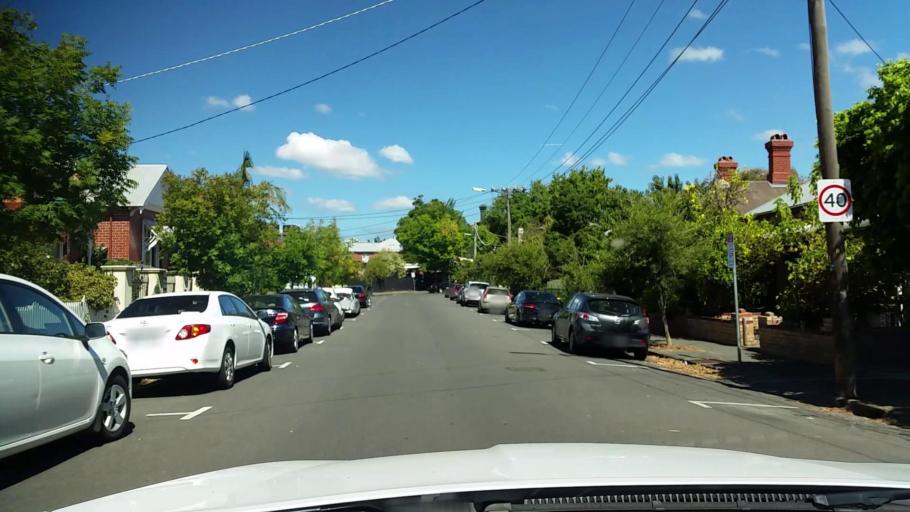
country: AU
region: Victoria
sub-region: Stonnington
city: Windsor
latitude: -37.8576
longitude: 144.9901
